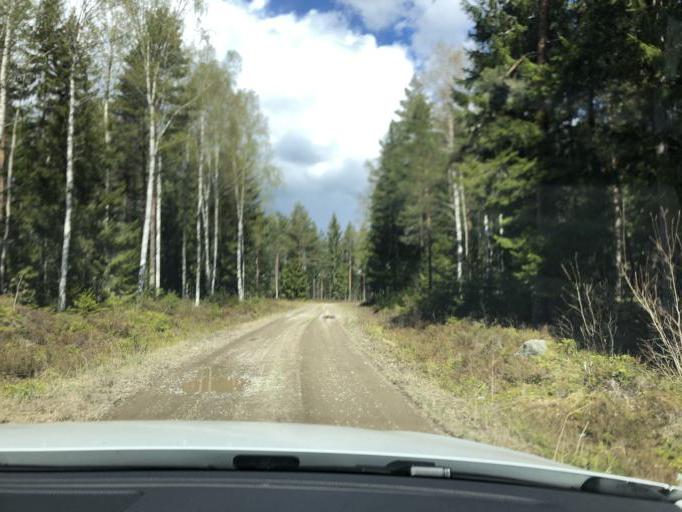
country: SE
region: Dalarna
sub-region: Avesta Kommun
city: Horndal
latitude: 60.2279
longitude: 16.5934
